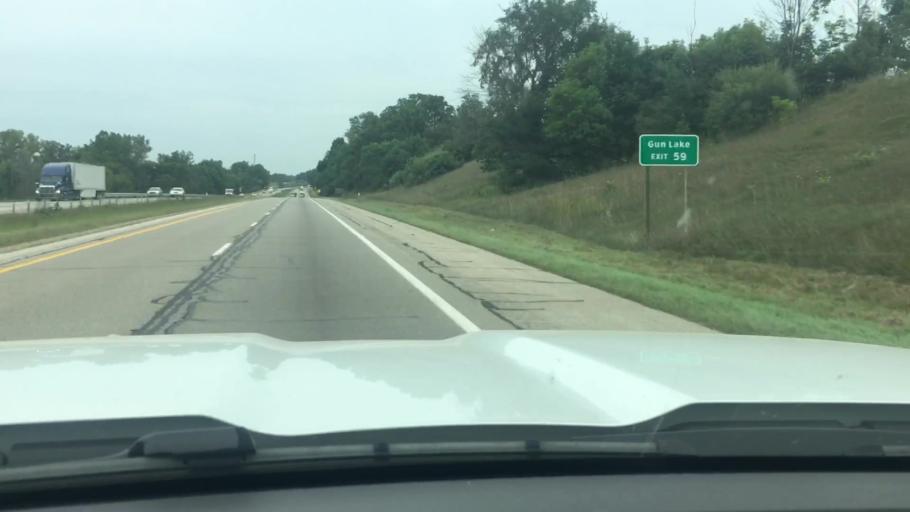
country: US
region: Michigan
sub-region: Allegan County
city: Wayland
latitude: 42.5808
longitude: -85.6625
